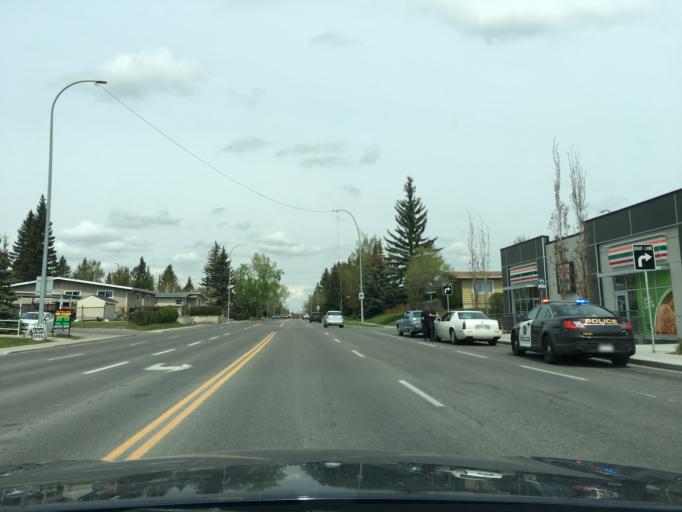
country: CA
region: Alberta
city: Calgary
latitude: 50.9638
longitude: -114.0848
